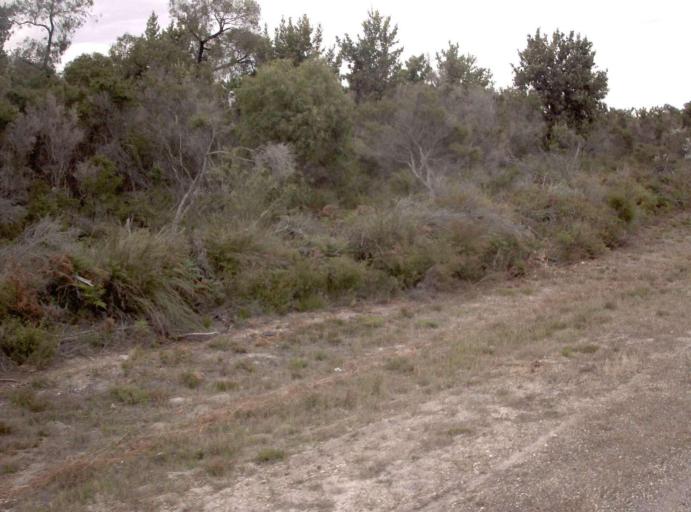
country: AU
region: Victoria
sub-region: Wellington
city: Sale
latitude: -38.1734
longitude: 147.3826
